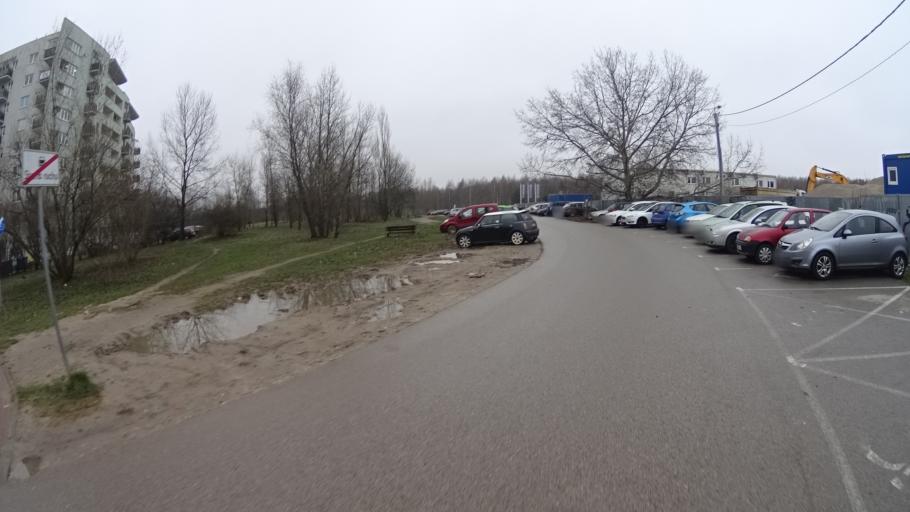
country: PL
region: Masovian Voivodeship
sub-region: Warszawa
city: Ursynow
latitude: 52.1389
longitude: 21.0389
